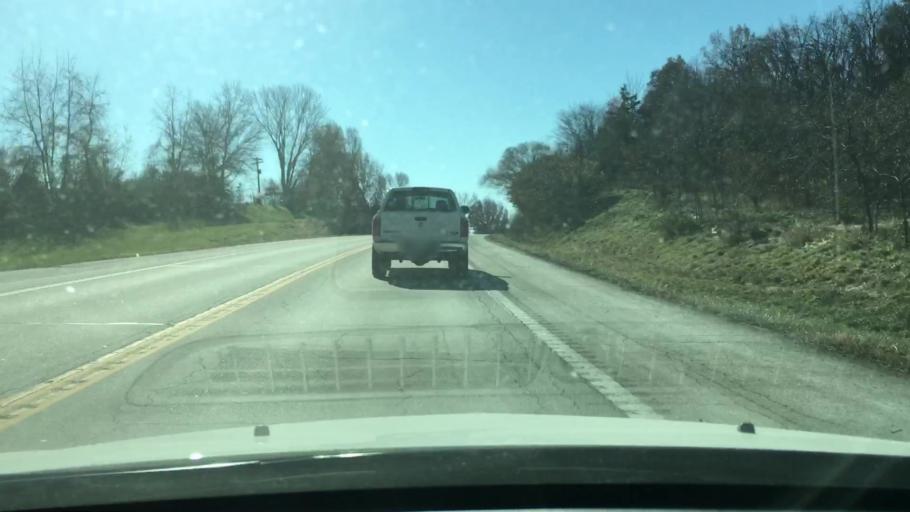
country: US
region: Missouri
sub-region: Pike County
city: Louisiana
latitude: 39.4340
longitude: -91.0802
